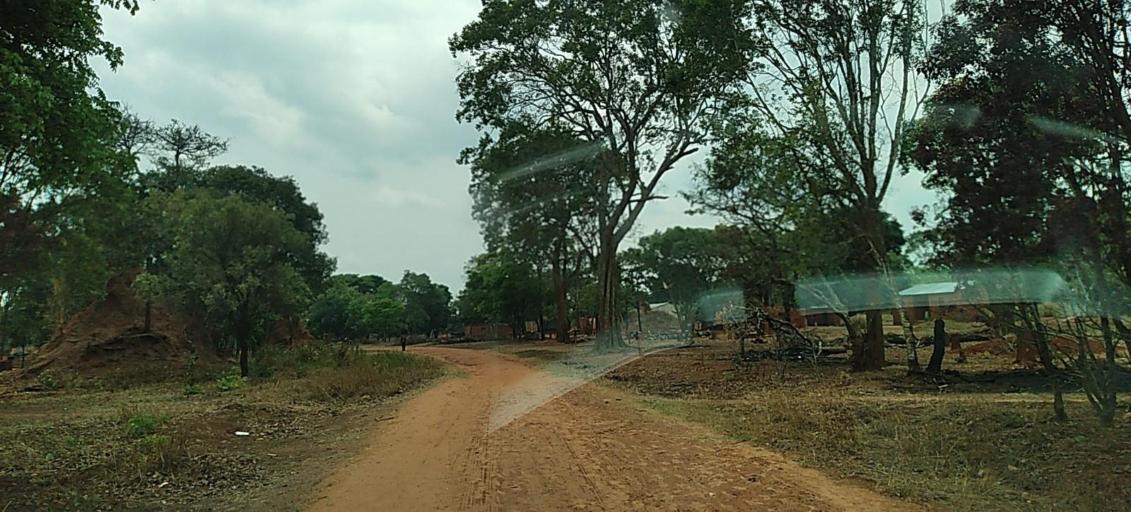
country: ZM
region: North-Western
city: Mwinilunga
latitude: -11.5189
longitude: 24.7897
